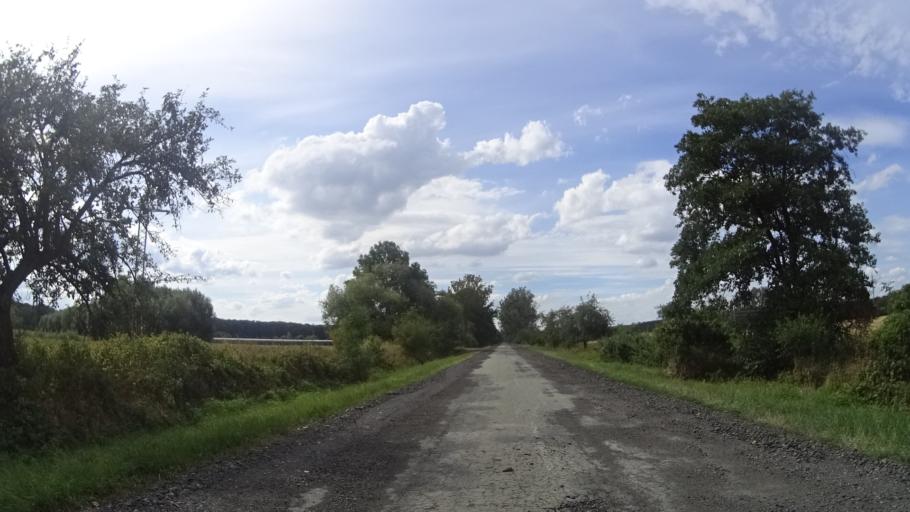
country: CZ
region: Olomoucky
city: Cervenka
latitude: 49.7149
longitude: 17.0522
